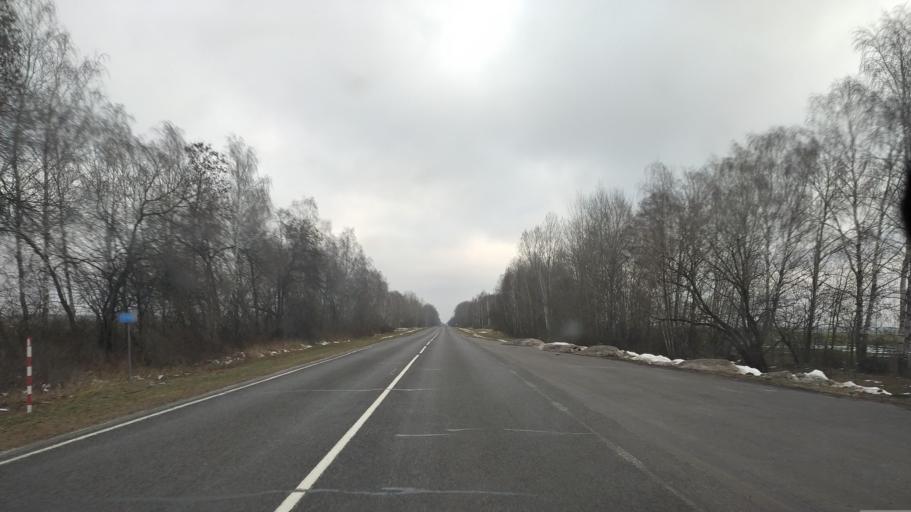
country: BY
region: Brest
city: Byaroza
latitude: 52.5016
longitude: 24.9193
